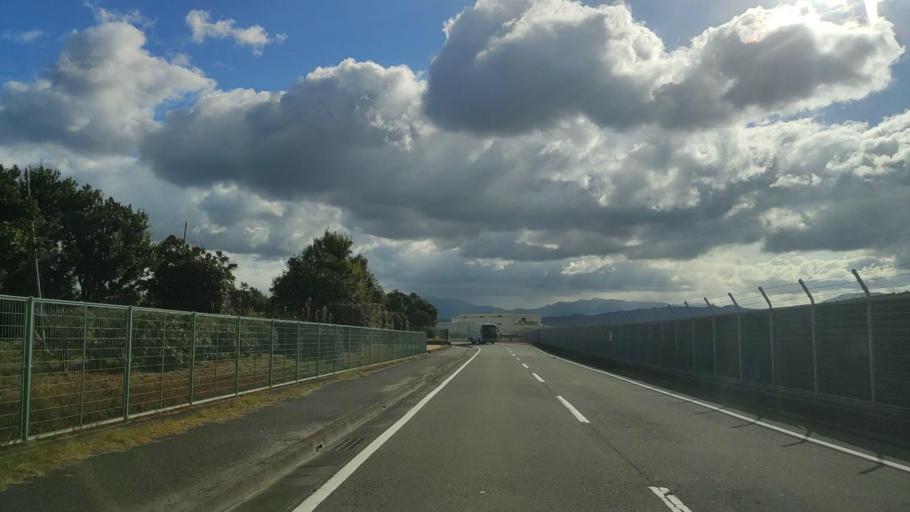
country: JP
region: Ehime
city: Masaki-cho
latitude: 33.8229
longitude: 132.7099
